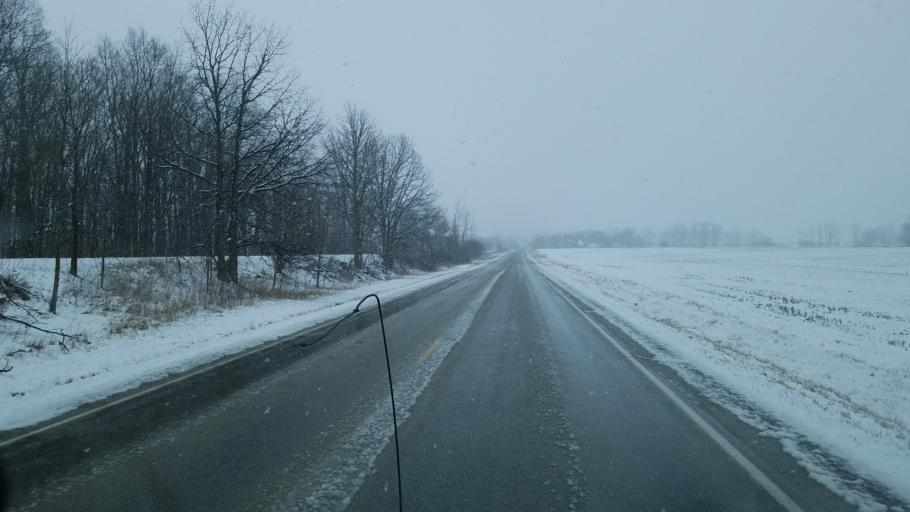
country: US
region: Indiana
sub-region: Randolph County
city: Lynn
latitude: 39.9718
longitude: -85.0429
